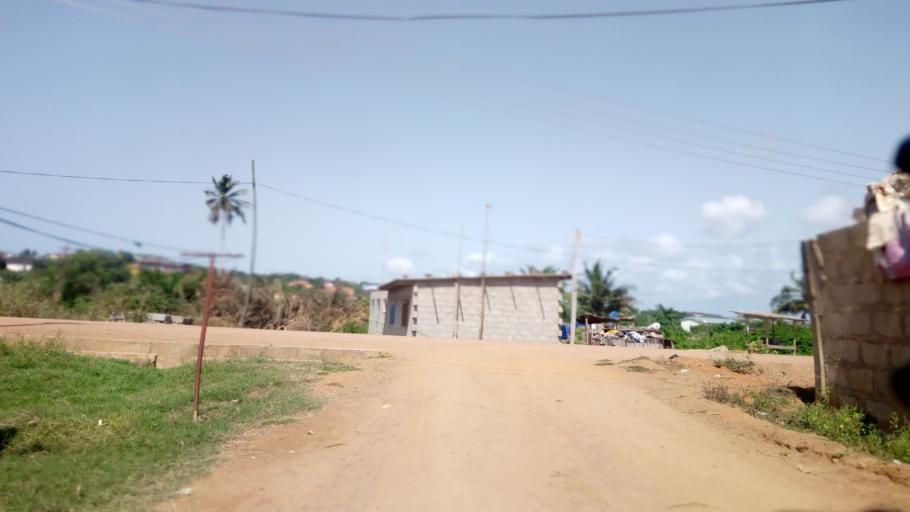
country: GH
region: Central
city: Cape Coast
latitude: 5.1125
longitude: -1.2679
